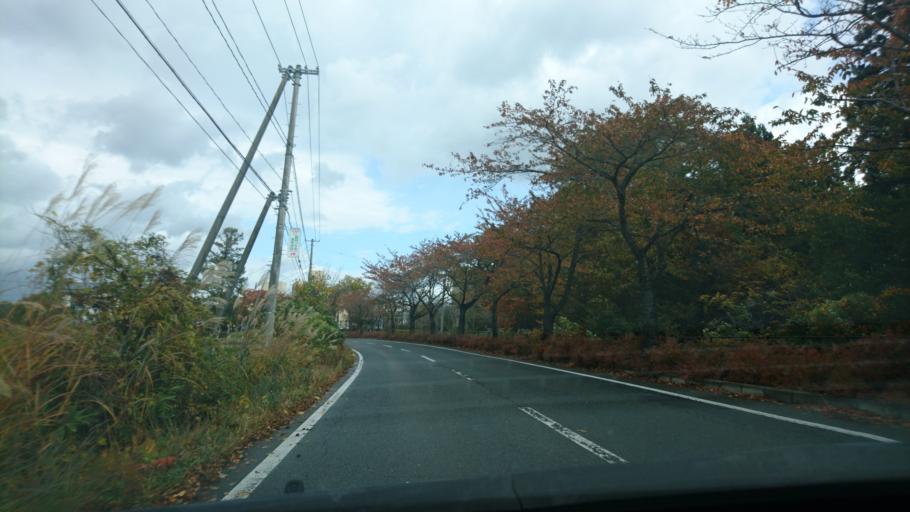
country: JP
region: Iwate
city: Shizukuishi
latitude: 39.6880
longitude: 141.0231
